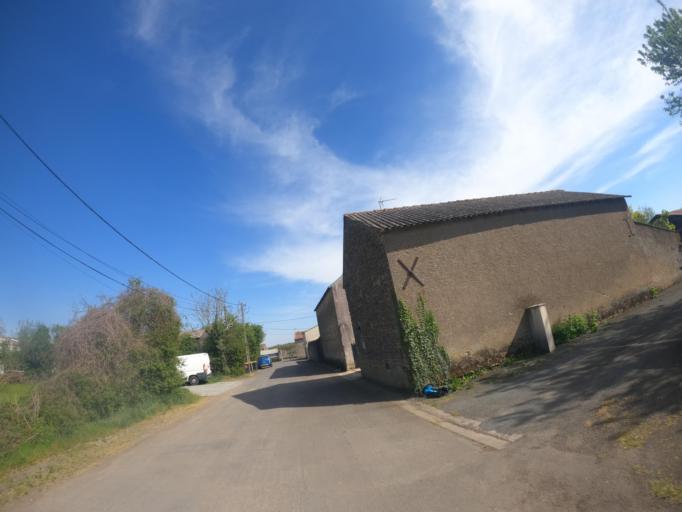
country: FR
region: Poitou-Charentes
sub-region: Departement des Deux-Sevres
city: Saint-Varent
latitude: 46.9120
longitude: -0.2133
